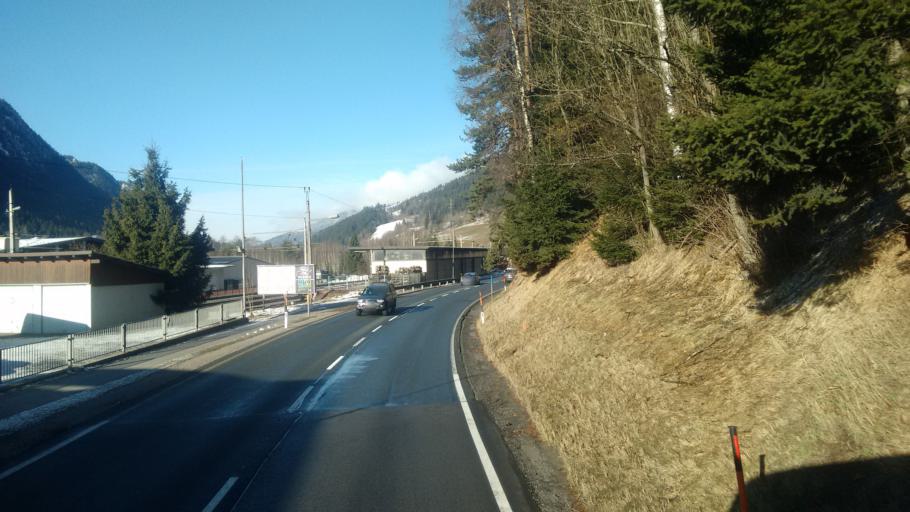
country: AT
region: Salzburg
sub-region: Politischer Bezirk Sankt Johann im Pongau
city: Forstau
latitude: 47.4041
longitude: 13.5714
